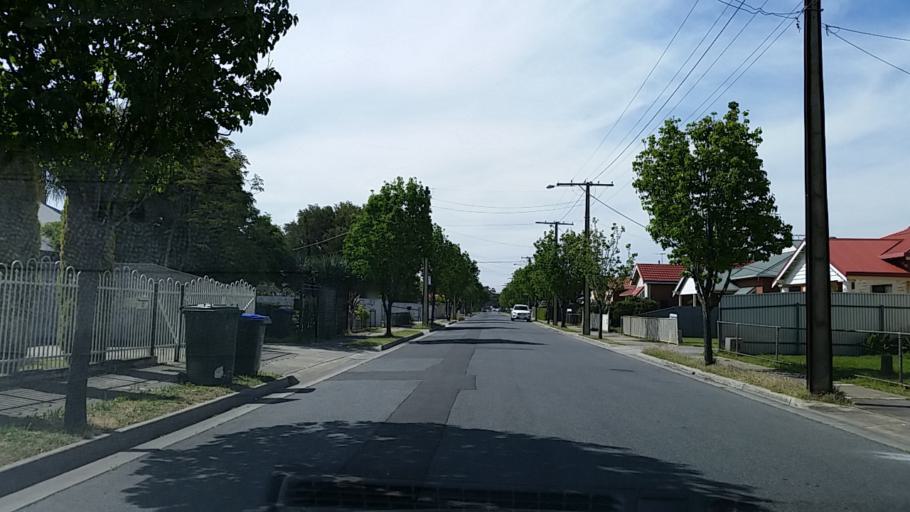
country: AU
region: South Australia
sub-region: Charles Sturt
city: Albert Park
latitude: -34.8743
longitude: 138.5188
